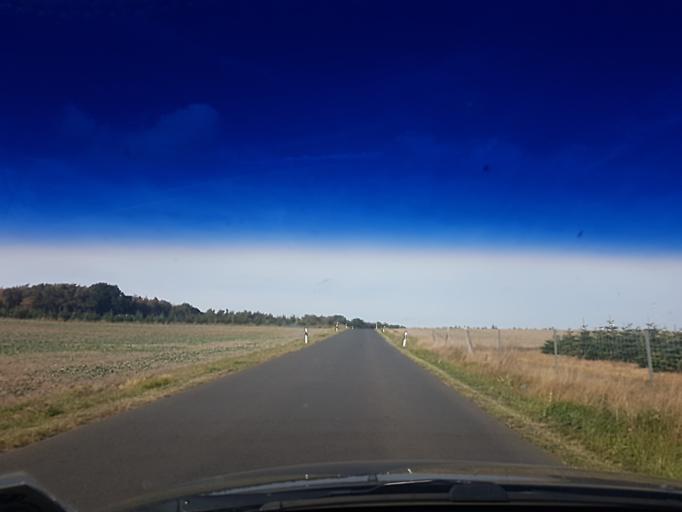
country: DE
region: Bavaria
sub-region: Upper Franconia
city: Schlusselfeld
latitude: 49.7608
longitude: 10.6435
